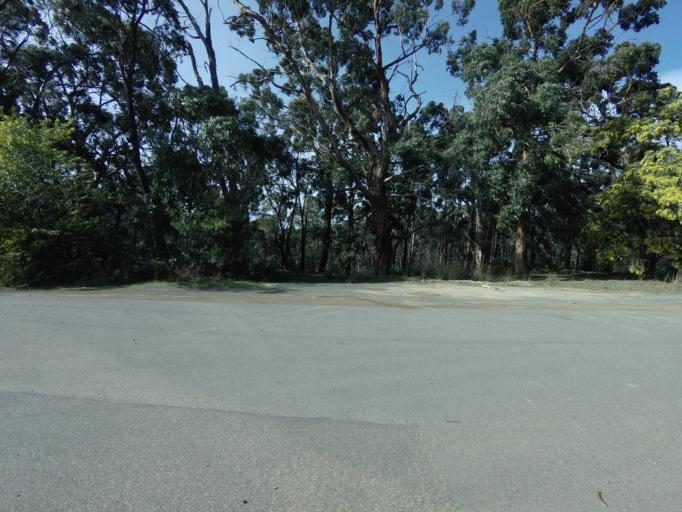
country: AU
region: Tasmania
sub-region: Kingborough
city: Margate
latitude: -43.0778
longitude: 147.2653
